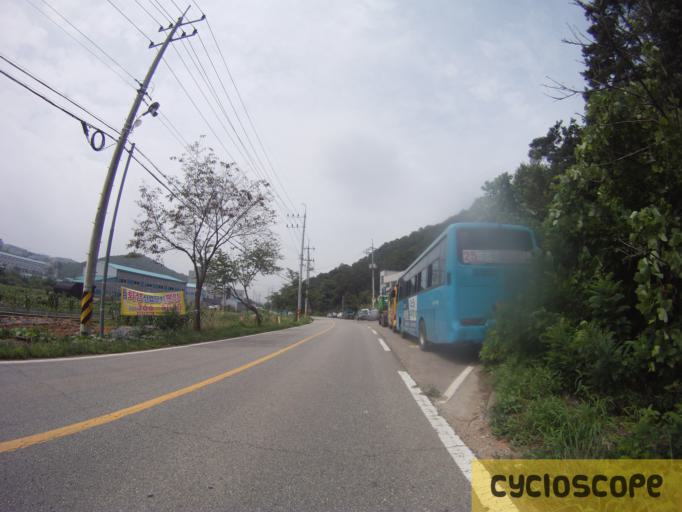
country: KR
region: Gyeonggi-do
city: Hwaseong-si
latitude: 37.1611
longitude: 126.9161
